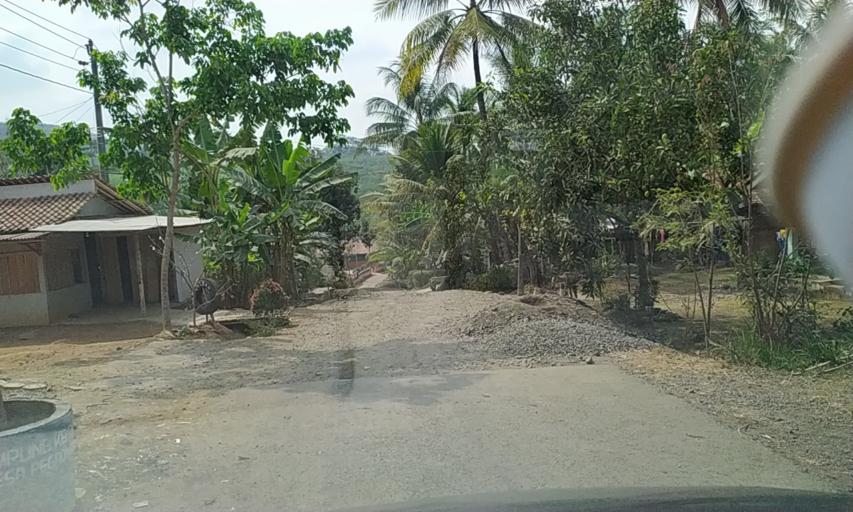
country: ID
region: Central Java
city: Gunungwilis
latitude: -7.4128
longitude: 108.7819
